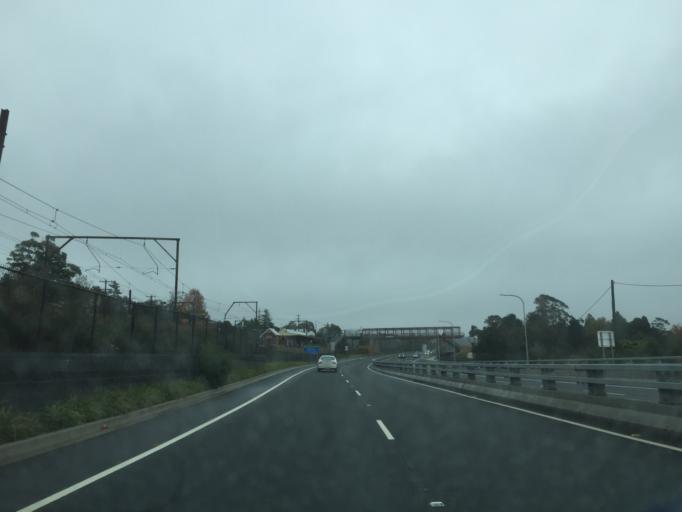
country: AU
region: New South Wales
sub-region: Blue Mountains Municipality
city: Hazelbrook
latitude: -33.7247
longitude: 150.4563
